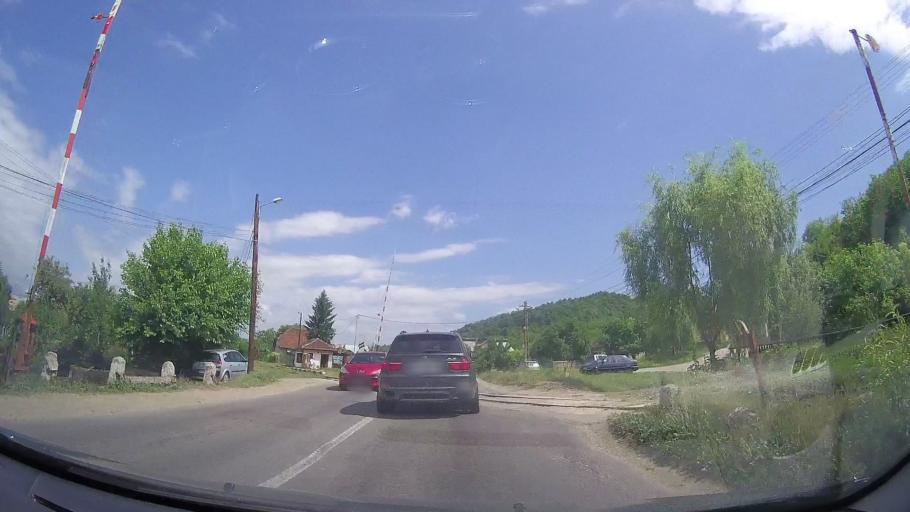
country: RO
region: Prahova
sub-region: Comuna Gura Vitioarei
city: Fagetu
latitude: 45.1248
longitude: 26.0355
